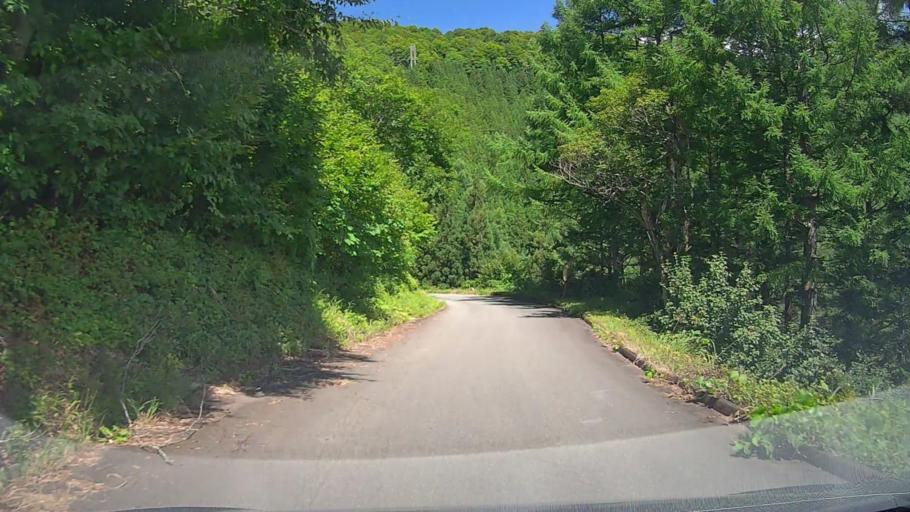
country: JP
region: Nagano
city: Iiyama
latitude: 36.9334
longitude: 138.4596
